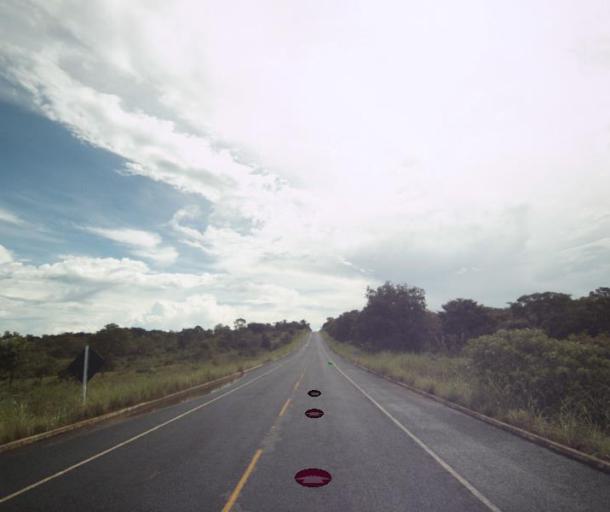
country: BR
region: Goias
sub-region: Sao Miguel Do Araguaia
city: Sao Miguel do Araguaia
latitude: -13.3025
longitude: -50.2735
